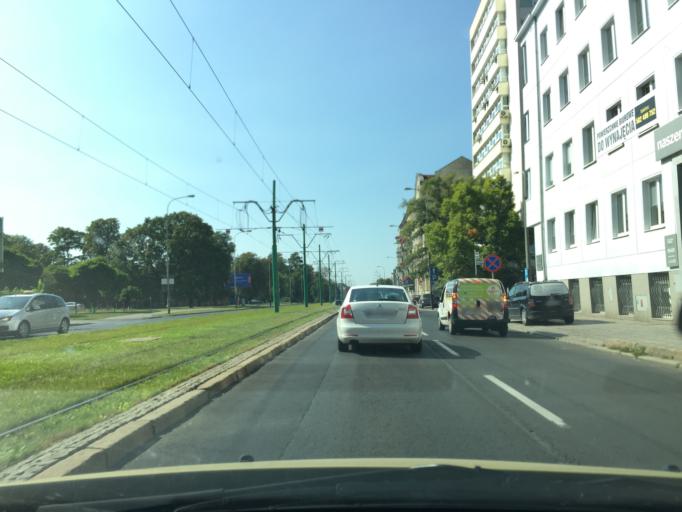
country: PL
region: Greater Poland Voivodeship
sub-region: Poznan
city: Poznan
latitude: 52.4051
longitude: 16.8986
